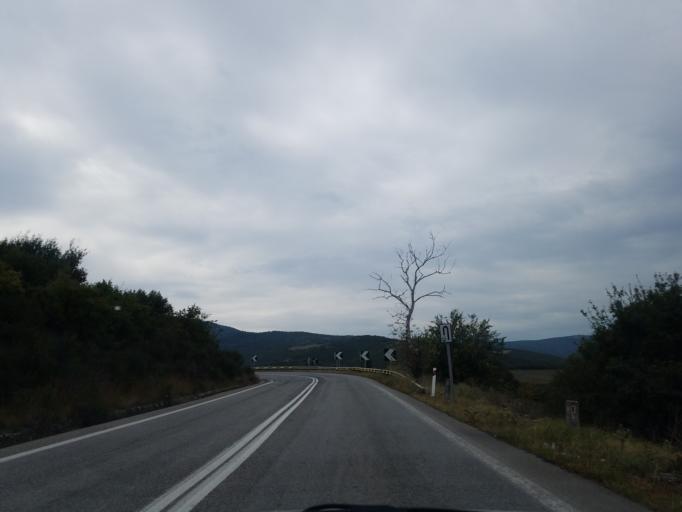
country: GR
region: Central Greece
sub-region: Nomos Fthiotidos
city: Domokos
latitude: 39.1518
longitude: 22.2974
